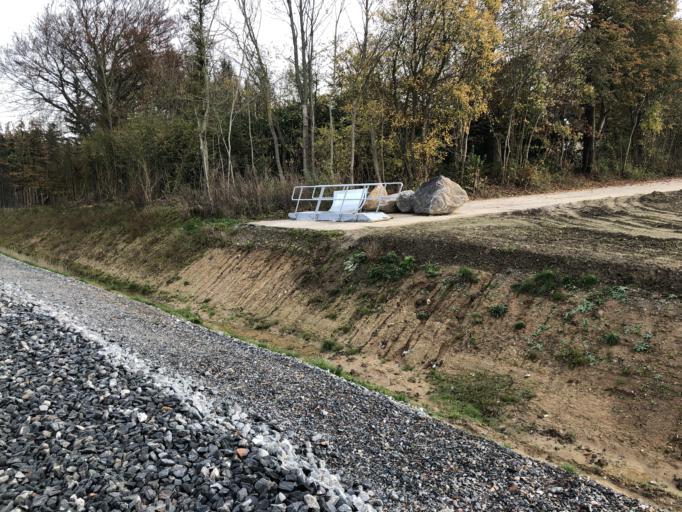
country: DK
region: Zealand
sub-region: Guldborgsund Kommune
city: Nykobing Falster
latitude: 54.7842
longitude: 11.8857
